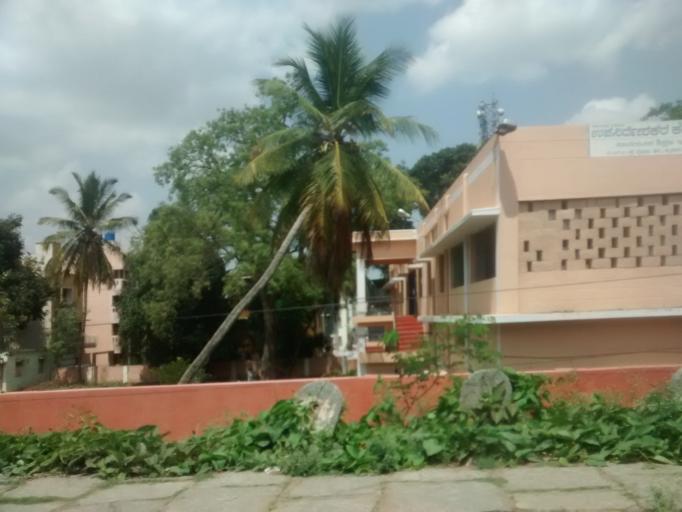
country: IN
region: Karnataka
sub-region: Mysore
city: Mysore
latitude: 12.3053
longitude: 76.6437
